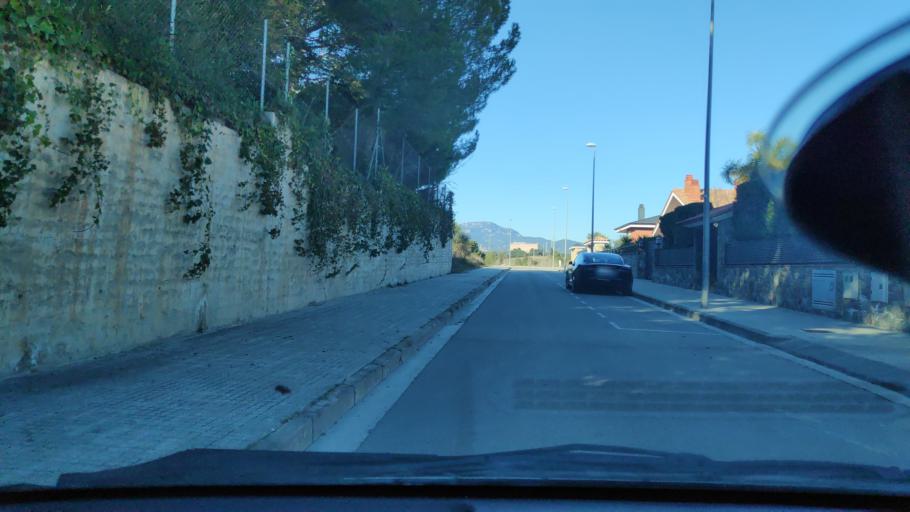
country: ES
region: Catalonia
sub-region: Provincia de Barcelona
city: Sant Quirze del Valles
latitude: 41.5358
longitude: 2.0590
